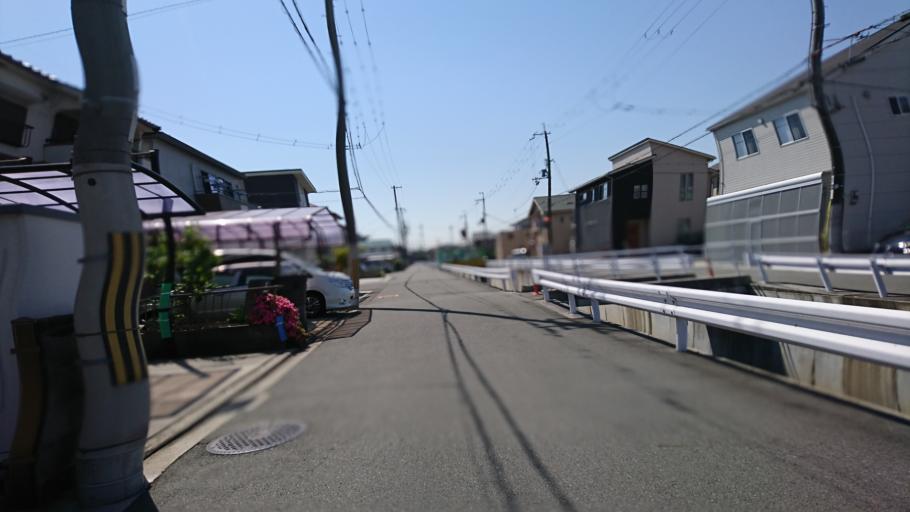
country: JP
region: Hyogo
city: Kakogawacho-honmachi
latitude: 34.7571
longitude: 134.8610
